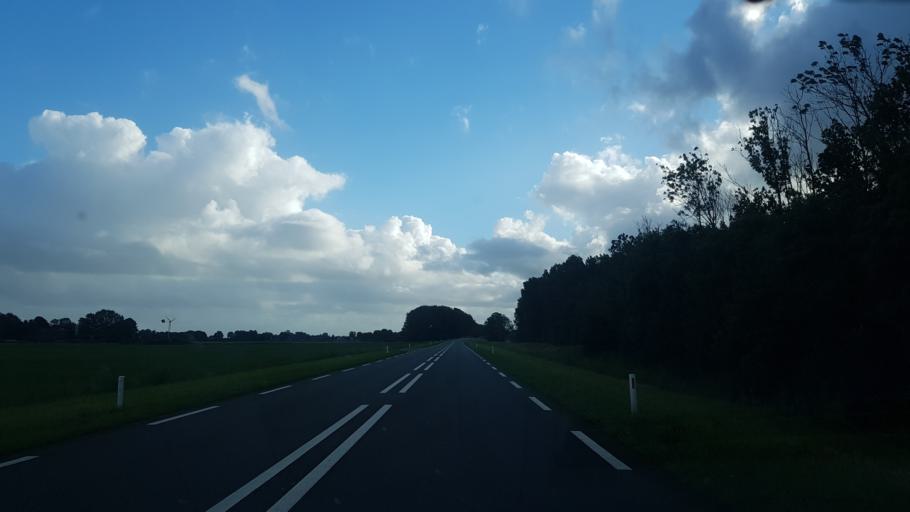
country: NL
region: Groningen
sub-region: Gemeente Slochteren
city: Slochteren
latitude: 53.3075
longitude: 6.7445
